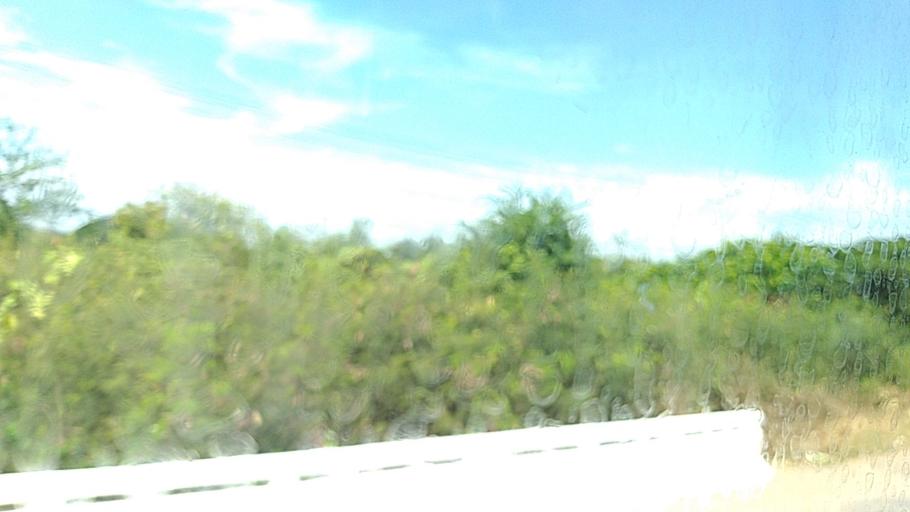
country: TH
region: Khon Kaen
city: Khon Kaen
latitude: 16.4222
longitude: 102.9169
